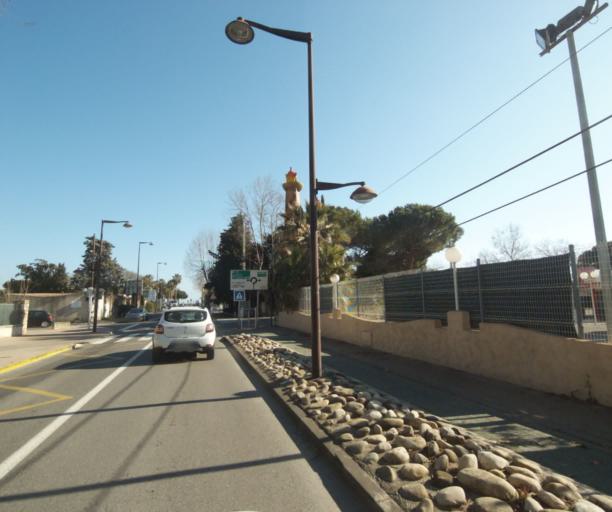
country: FR
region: Provence-Alpes-Cote d'Azur
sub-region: Departement des Alpes-Maritimes
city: Biot
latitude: 43.6131
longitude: 7.1241
